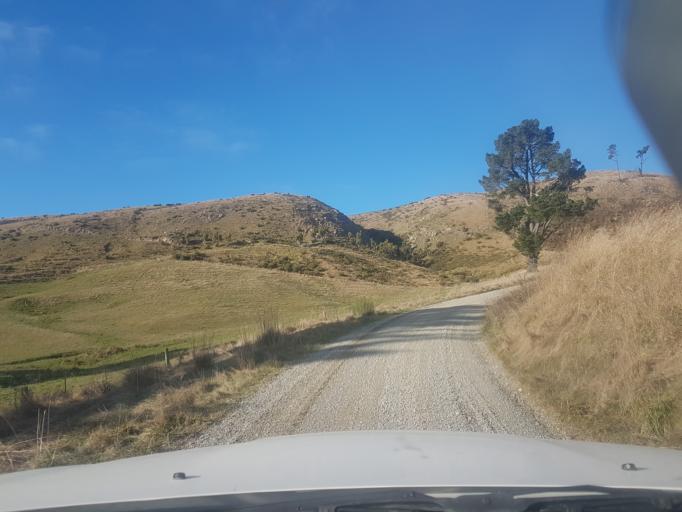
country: NZ
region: Canterbury
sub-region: Timaru District
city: Pleasant Point
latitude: -44.1653
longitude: 170.8778
